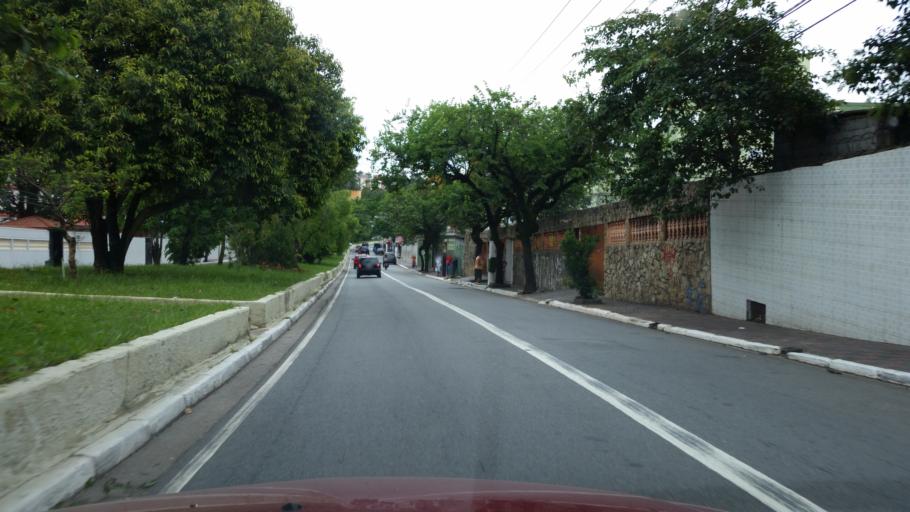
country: BR
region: Sao Paulo
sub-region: Ferraz De Vasconcelos
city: Ferraz de Vasconcelos
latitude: -23.5509
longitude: -46.4392
